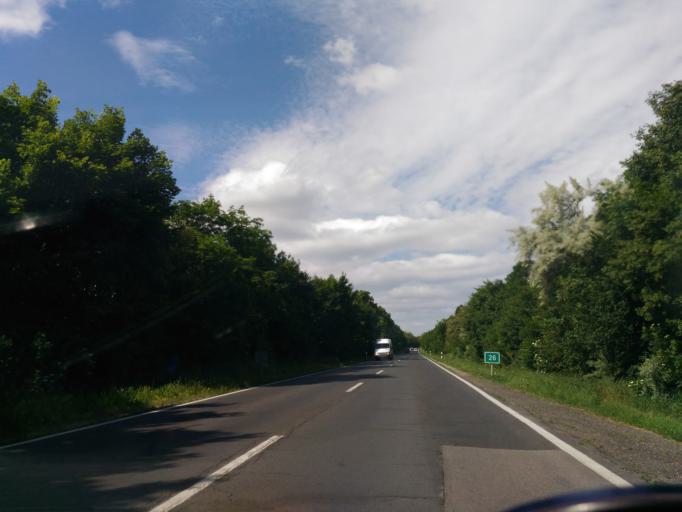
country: HU
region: Pest
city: Tarnok
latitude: 47.3507
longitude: 18.8530
